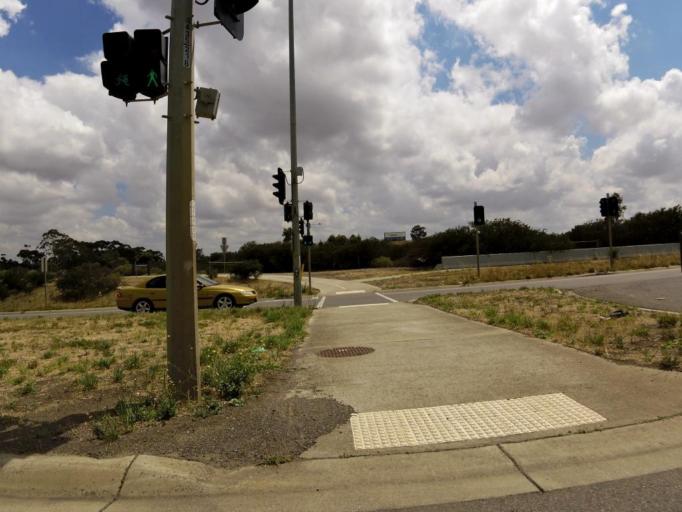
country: AU
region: Victoria
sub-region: Hume
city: Craigieburn
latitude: -37.6010
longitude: 144.9569
